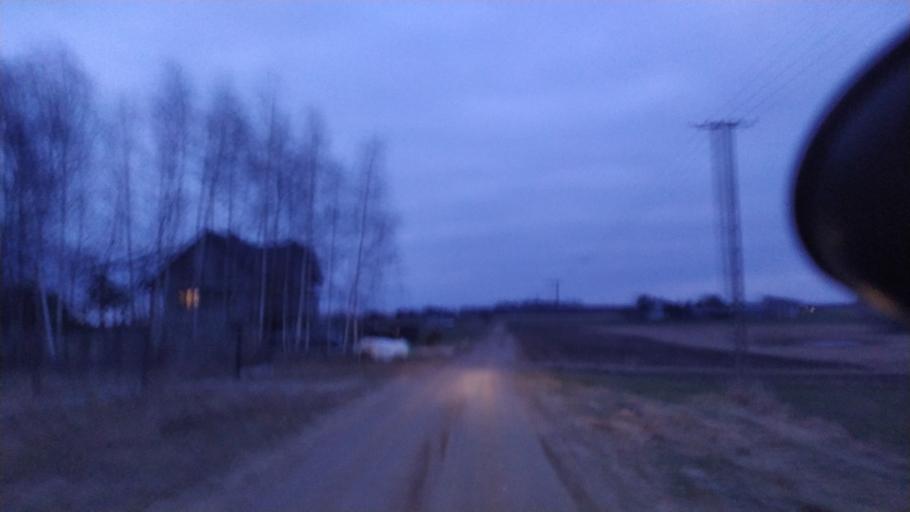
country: PL
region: Lublin Voivodeship
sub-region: Powiat lubartowski
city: Kamionka
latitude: 51.3933
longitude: 22.4227
